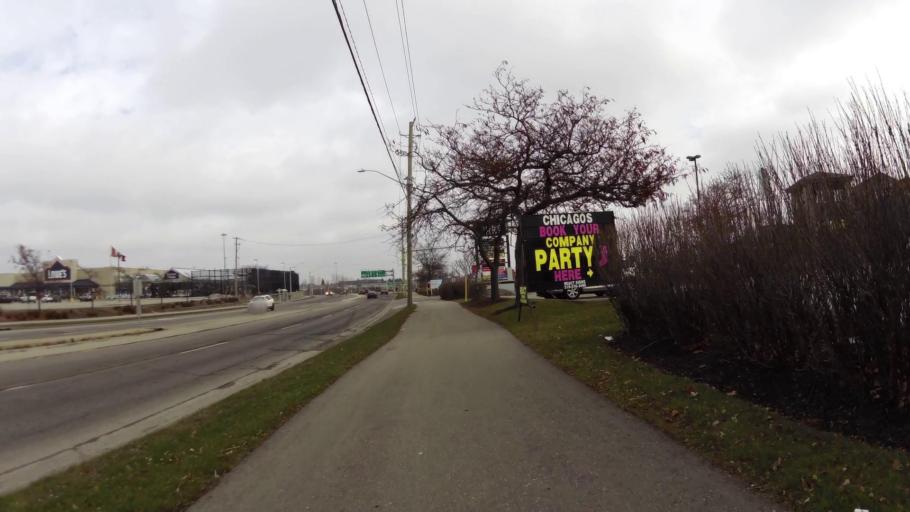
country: CA
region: Ontario
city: Kitchener
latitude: 43.4238
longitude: -80.4850
